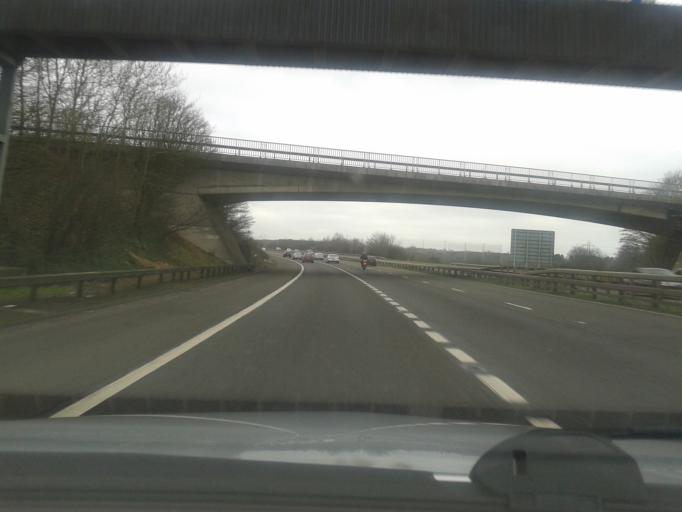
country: GB
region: England
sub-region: South Gloucestershire
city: Stoke Gifford
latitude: 51.5104
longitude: -2.5228
